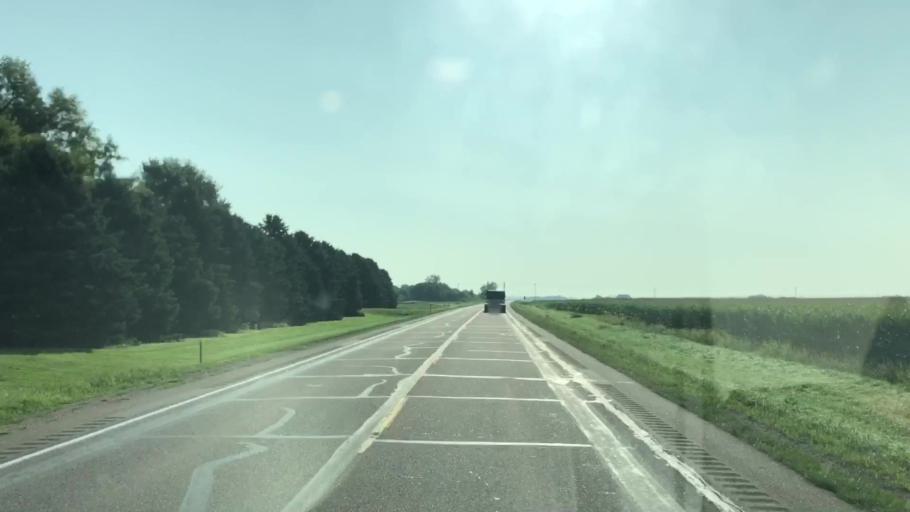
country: US
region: Iowa
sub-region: O'Brien County
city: Sheldon
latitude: 43.1860
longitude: -95.9662
